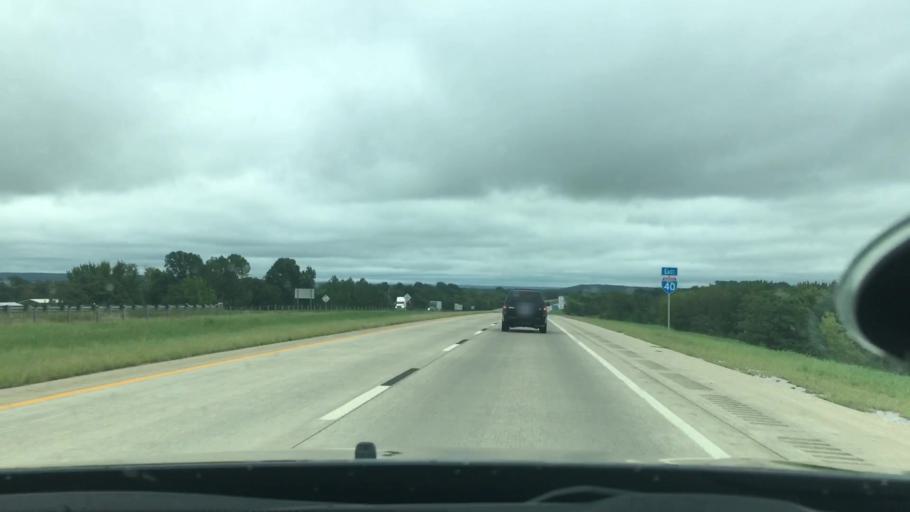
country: US
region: Oklahoma
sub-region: Muskogee County
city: Warner
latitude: 35.4789
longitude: -95.2966
